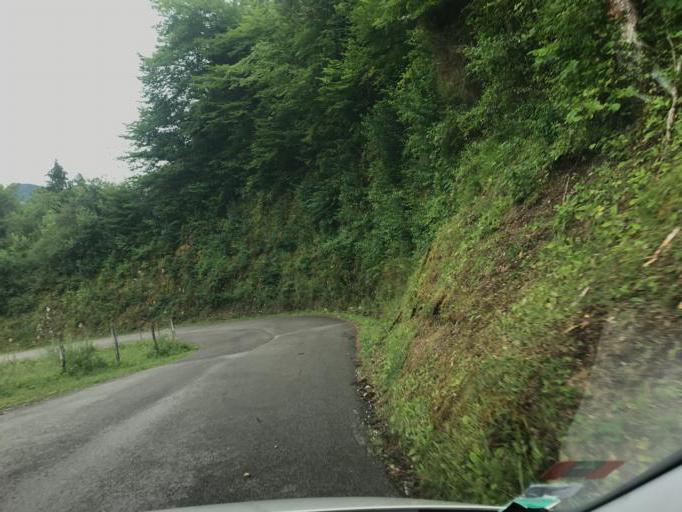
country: FR
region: Franche-Comte
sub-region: Departement du Jura
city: Saint-Claude
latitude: 46.3634
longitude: 5.8662
